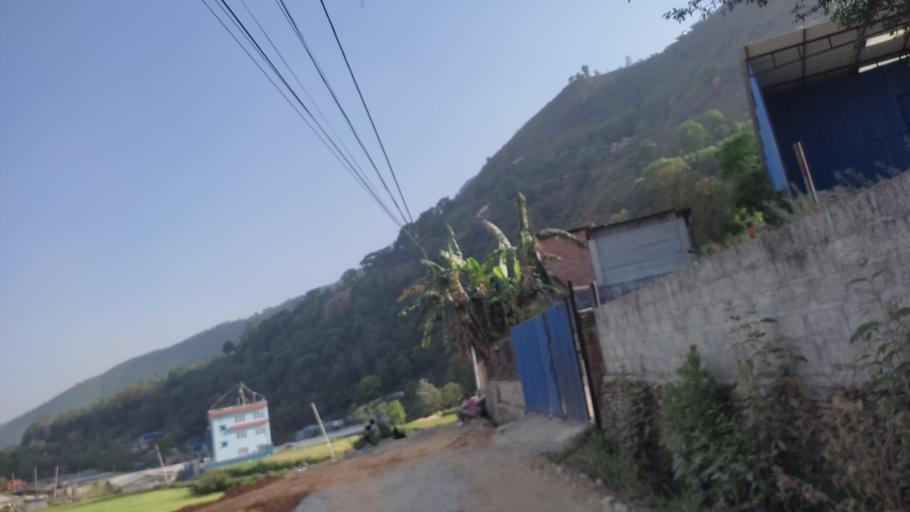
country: NP
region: Central Region
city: Kirtipur
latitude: 27.6572
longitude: 85.2712
